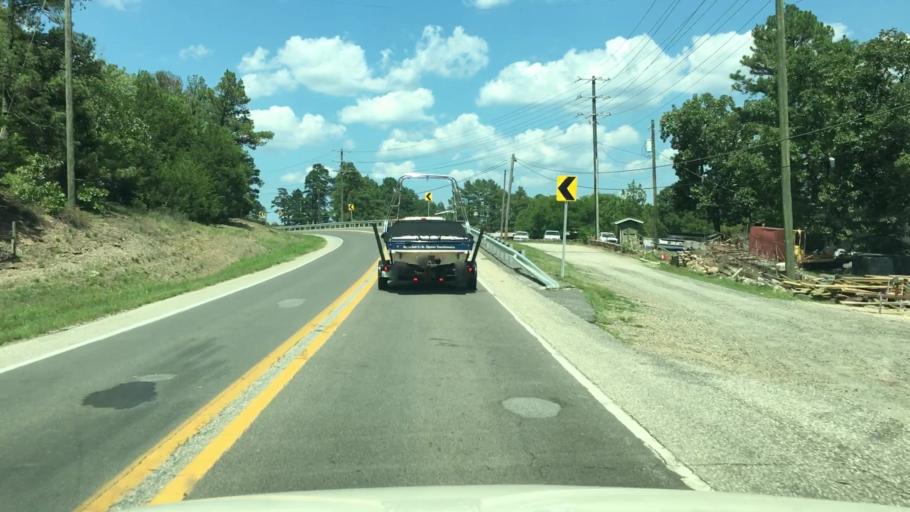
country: US
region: Arkansas
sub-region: Garland County
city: Lake Hamilton
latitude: 34.4043
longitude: -93.0917
